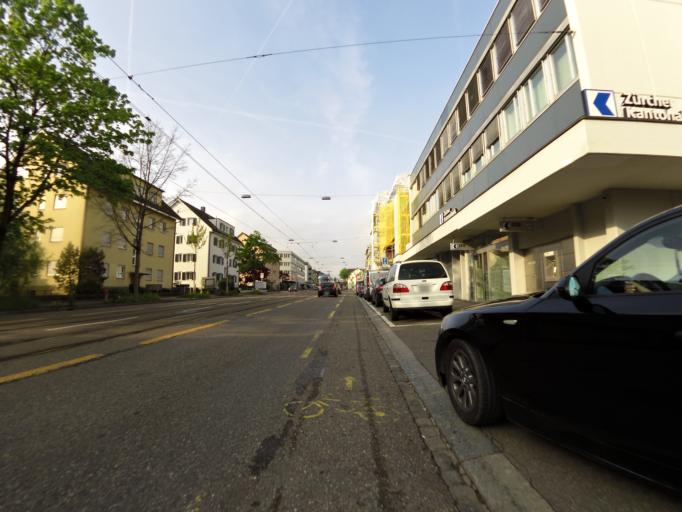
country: CH
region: Zurich
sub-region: Bezirk Zuerich
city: Zuerich (Kreis 11) / Seebach
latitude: 47.4208
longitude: 8.5492
